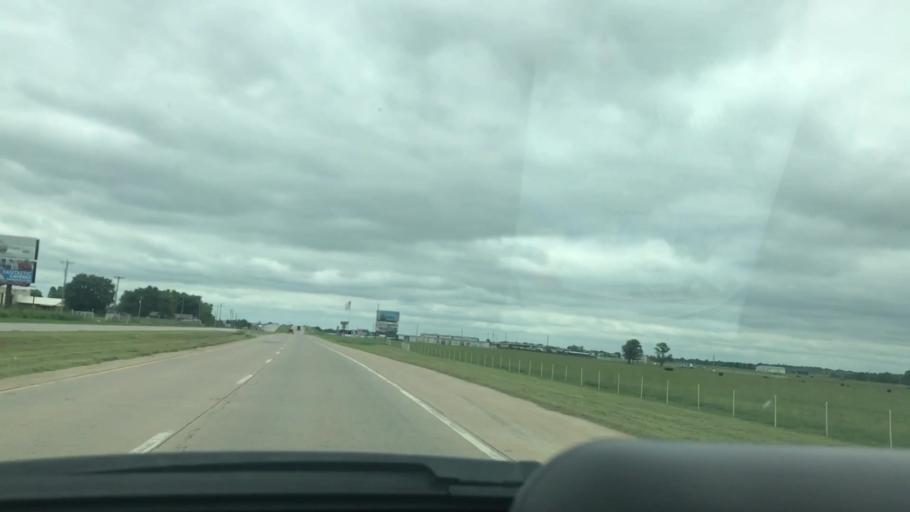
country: US
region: Oklahoma
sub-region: Craig County
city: Vinita
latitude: 36.5489
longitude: -95.2201
